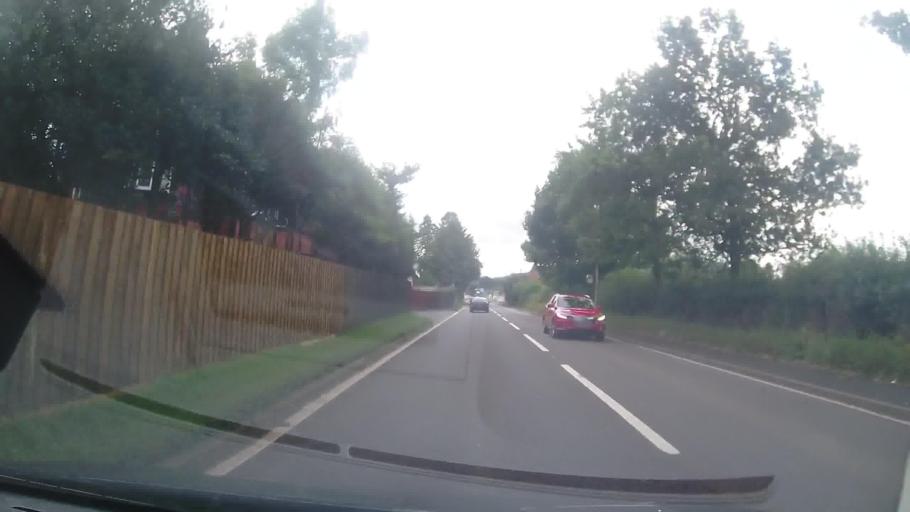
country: GB
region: England
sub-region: Shropshire
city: Craven Arms
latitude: 52.4487
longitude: -2.8380
